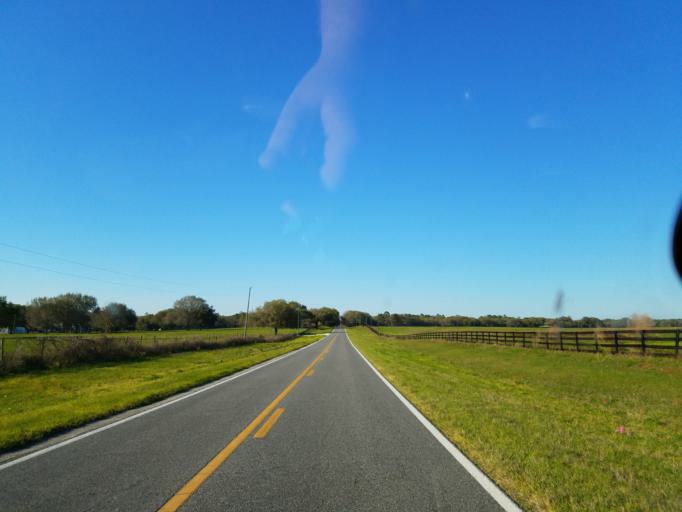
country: US
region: Florida
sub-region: Suwannee County
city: Wellborn
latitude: 30.1367
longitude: -82.8872
